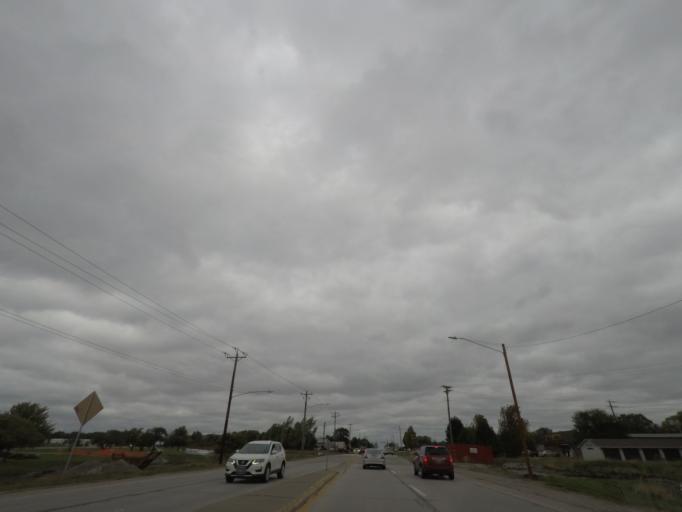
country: US
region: Iowa
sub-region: Polk County
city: Ankeny
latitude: 41.7202
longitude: -93.6004
